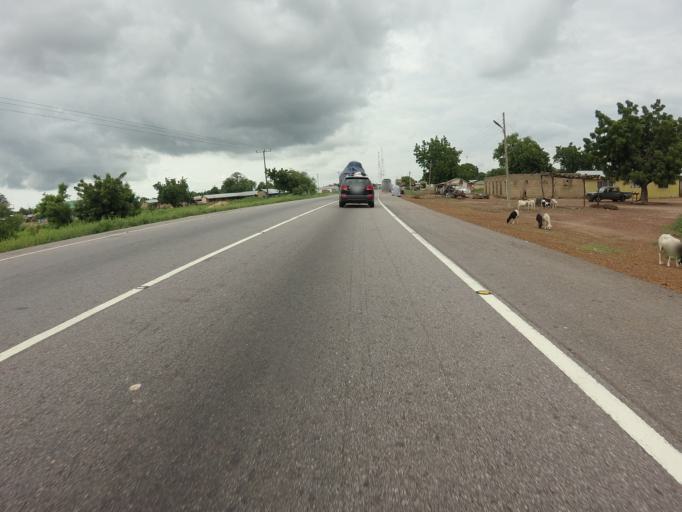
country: GH
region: Northern
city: Tamale
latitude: 9.1213
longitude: -1.2759
